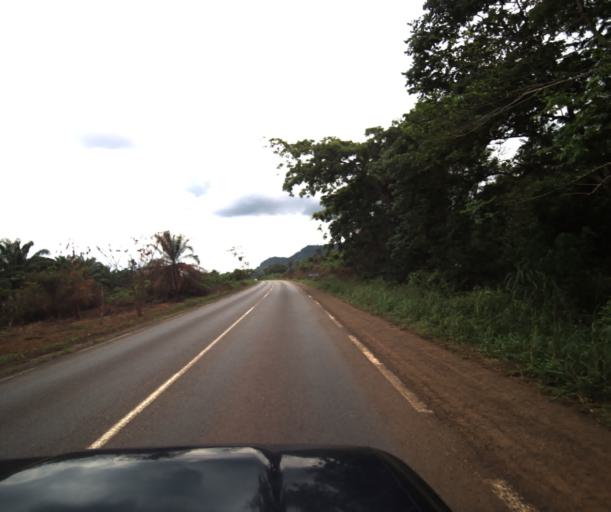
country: CM
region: Centre
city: Eseka
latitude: 3.8918
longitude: 10.7796
